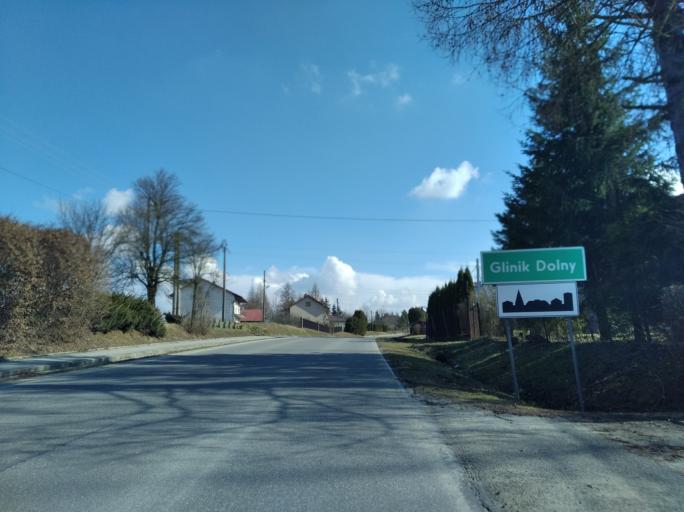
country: PL
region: Subcarpathian Voivodeship
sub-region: Powiat strzyzowski
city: Frysztak
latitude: 49.8430
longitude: 21.5868
